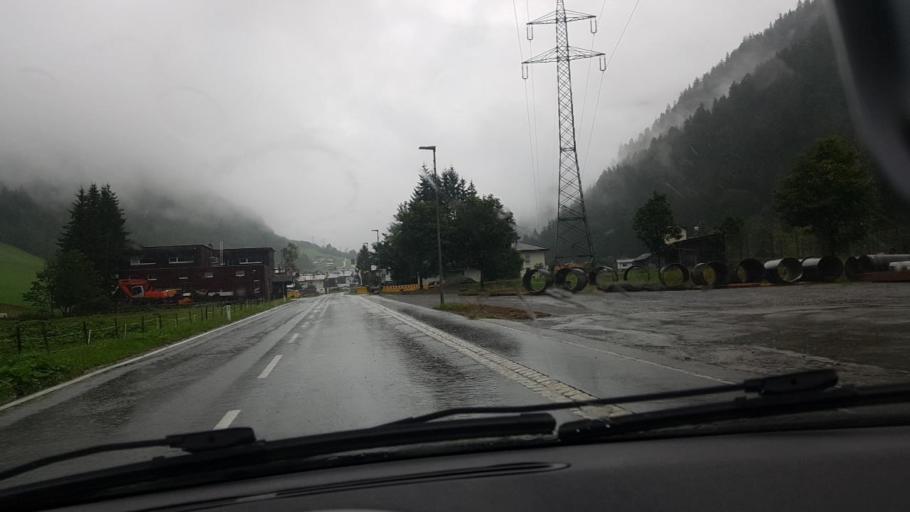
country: AT
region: Vorarlberg
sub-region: Politischer Bezirk Bludenz
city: Klosterle
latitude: 47.1315
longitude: 10.0818
